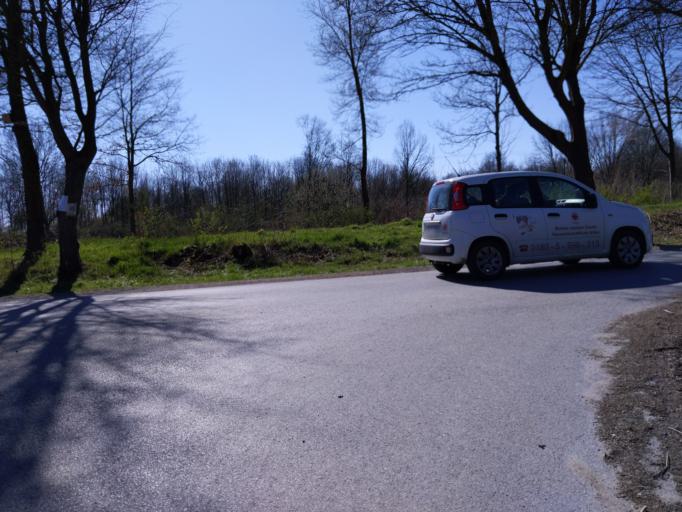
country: DE
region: North Rhine-Westphalia
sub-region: Regierungsbezirk Dusseldorf
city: Schermbeck
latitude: 51.6714
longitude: 6.8664
